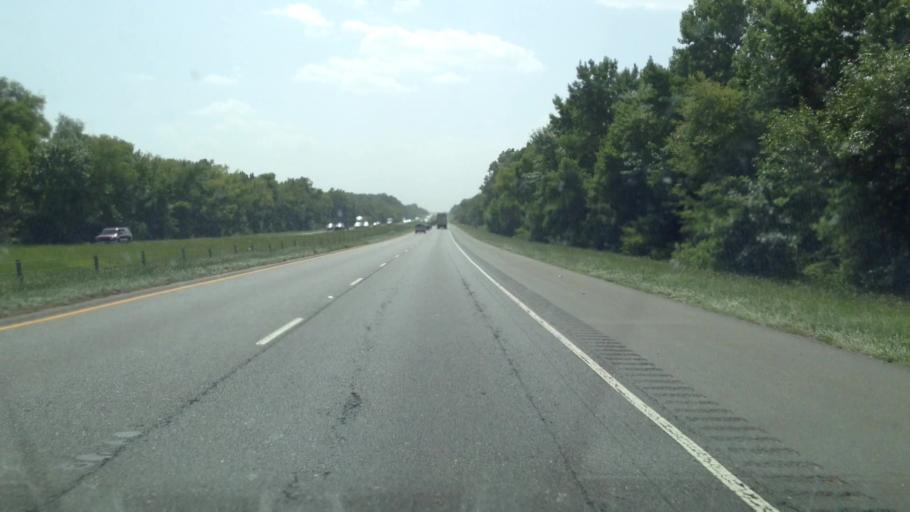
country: US
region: Louisiana
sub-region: Bossier Parish
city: Eastwood
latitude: 32.5422
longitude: -93.5751
